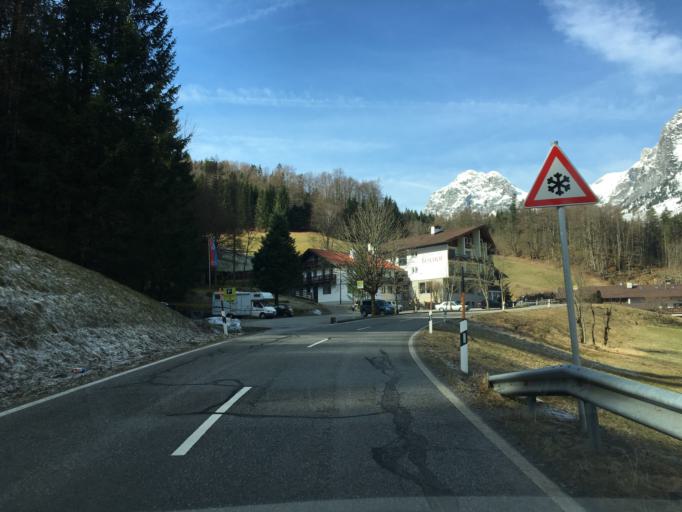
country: DE
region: Bavaria
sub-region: Upper Bavaria
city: Ramsau
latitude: 47.6057
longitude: 12.8708
